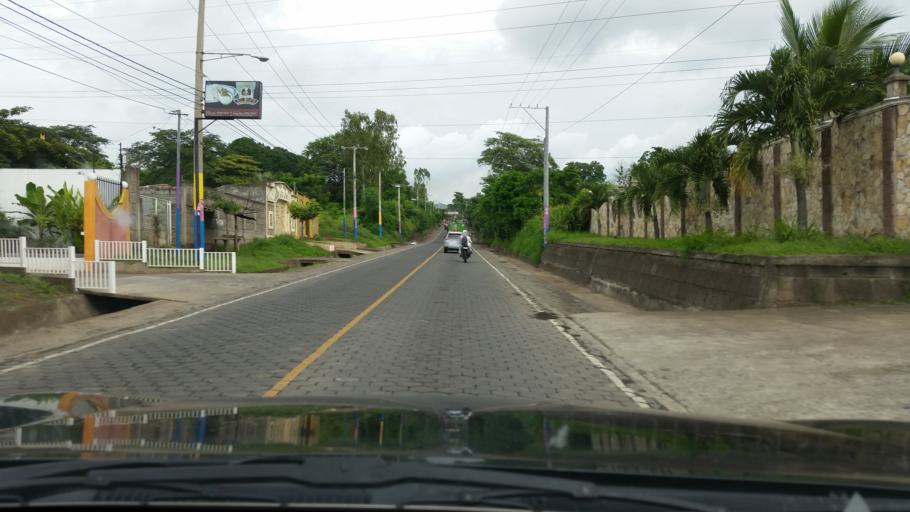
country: NI
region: Masaya
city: Ticuantepe
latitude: 12.0277
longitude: -86.2073
